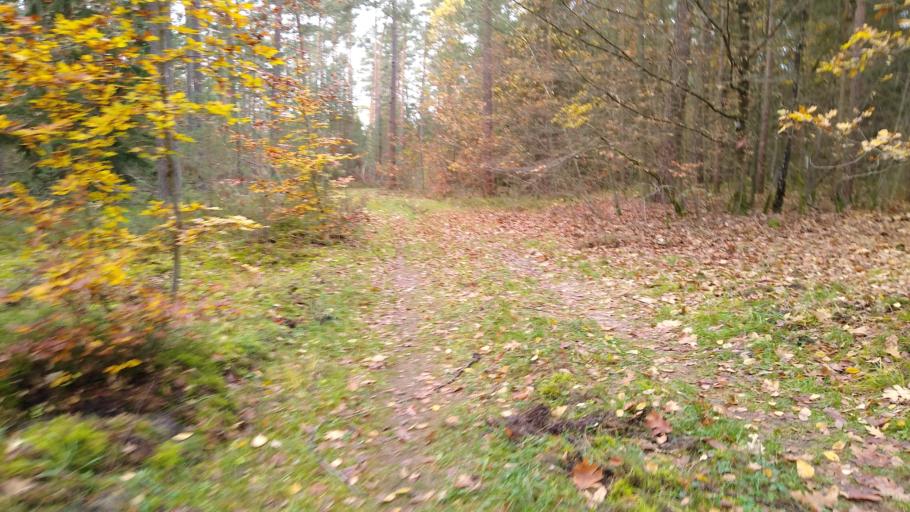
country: DE
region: Bavaria
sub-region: Regierungsbezirk Mittelfranken
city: Kalchreuth
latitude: 49.5413
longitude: 11.1019
